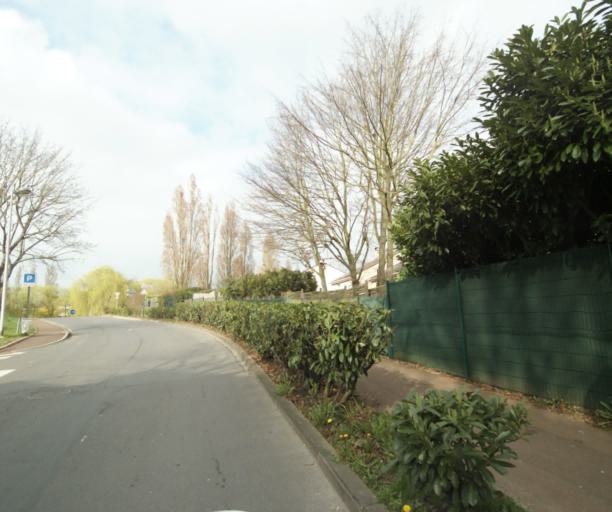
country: FR
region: Ile-de-France
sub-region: Departement du Val-d'Oise
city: Vaureal
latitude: 49.0472
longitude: 2.0450
